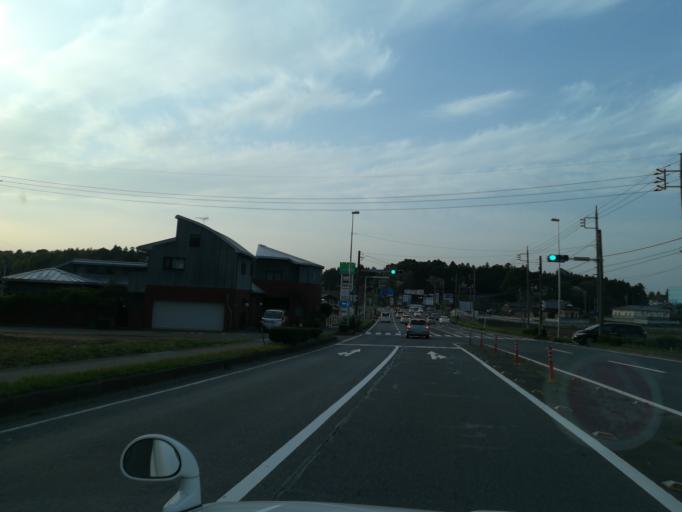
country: JP
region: Ibaraki
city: Naka
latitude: 36.0609
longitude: 140.0827
